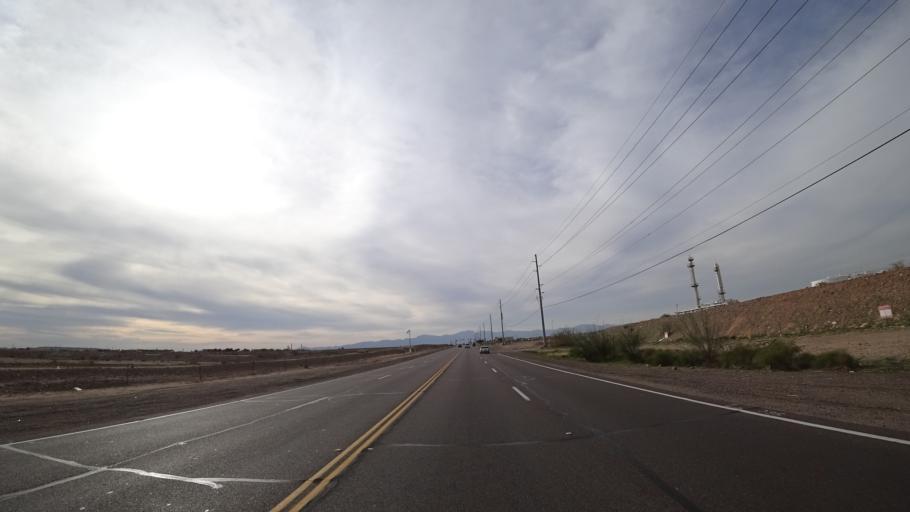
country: US
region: Arizona
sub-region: Maricopa County
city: Youngtown
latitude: 33.5654
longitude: -112.3190
